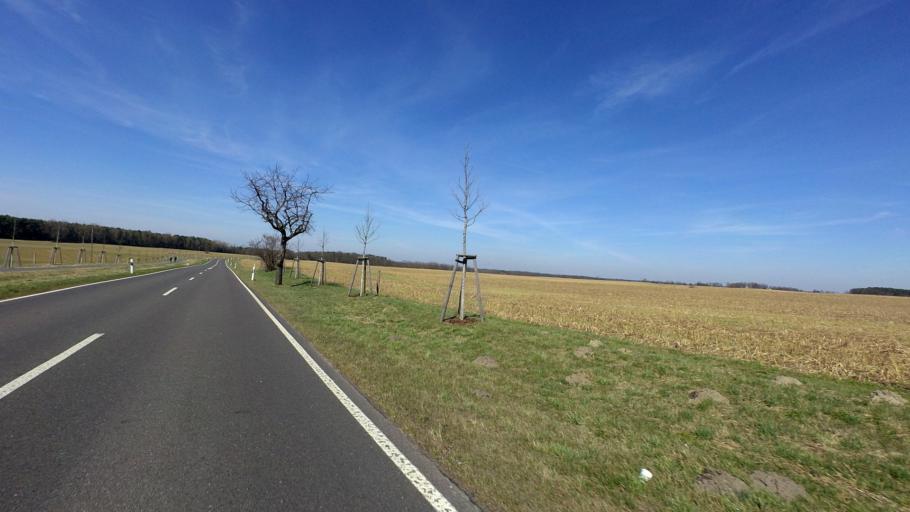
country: DE
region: Brandenburg
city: Furstenwalde
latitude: 52.3920
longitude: 14.0480
